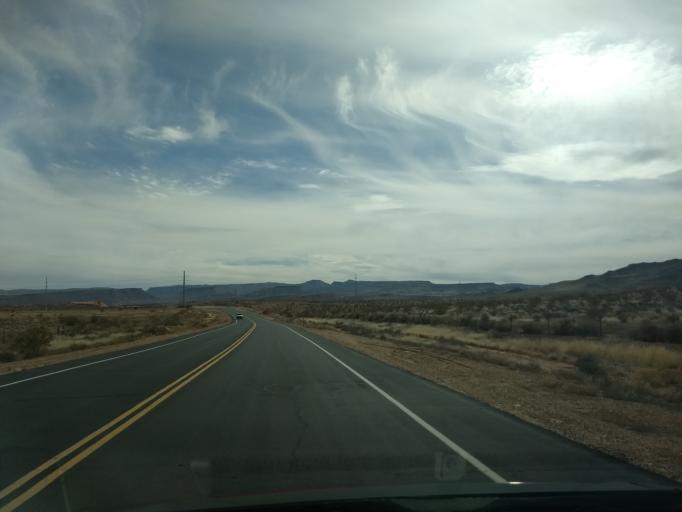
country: US
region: Utah
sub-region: Washington County
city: Washington
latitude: 37.0177
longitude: -113.4993
